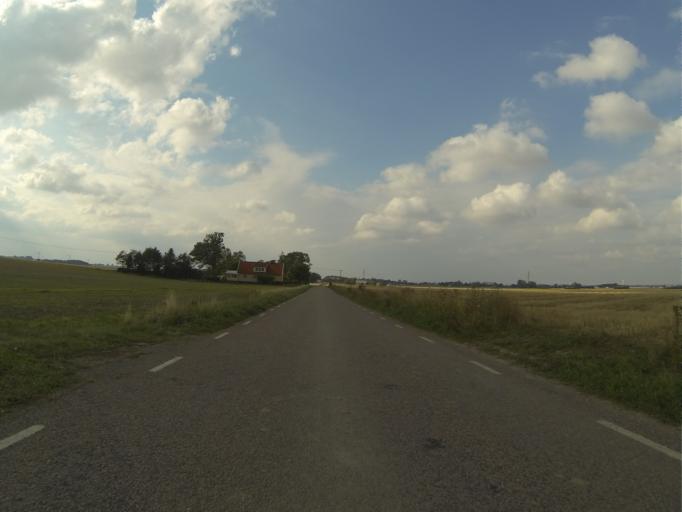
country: SE
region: Skane
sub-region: Lunds Kommun
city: Lund
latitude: 55.7558
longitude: 13.1929
